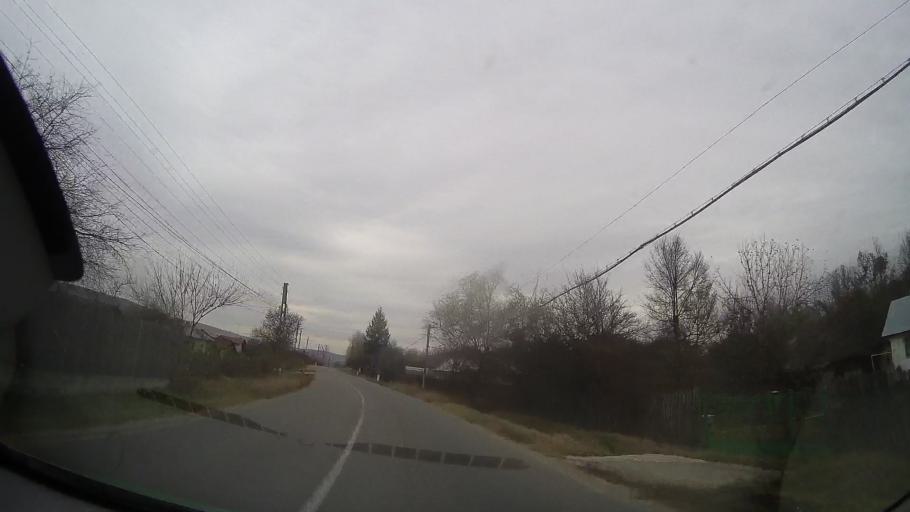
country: RO
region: Prahova
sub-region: Comuna Iordachianu
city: Iordacheanu
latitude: 45.0334
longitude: 26.2408
